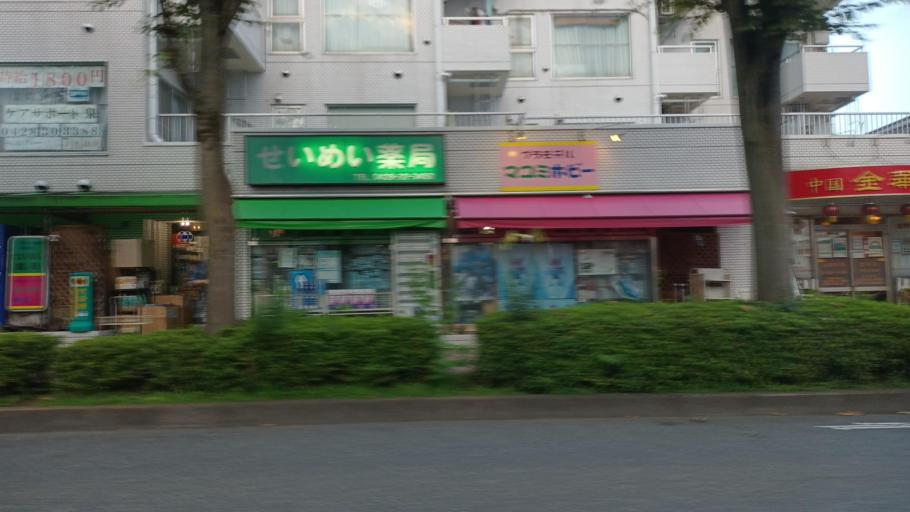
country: JP
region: Tokyo
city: Fussa
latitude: 35.7863
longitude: 139.3031
